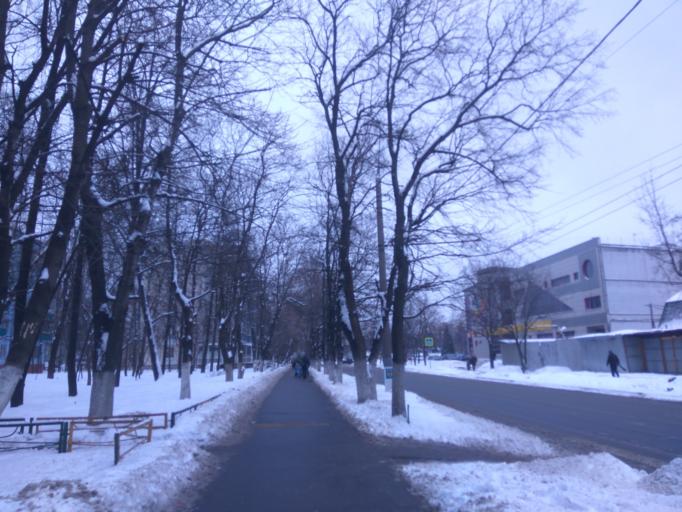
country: RU
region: Moscow
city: Novyye Kuz'minki
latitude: 55.7017
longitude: 37.7656
